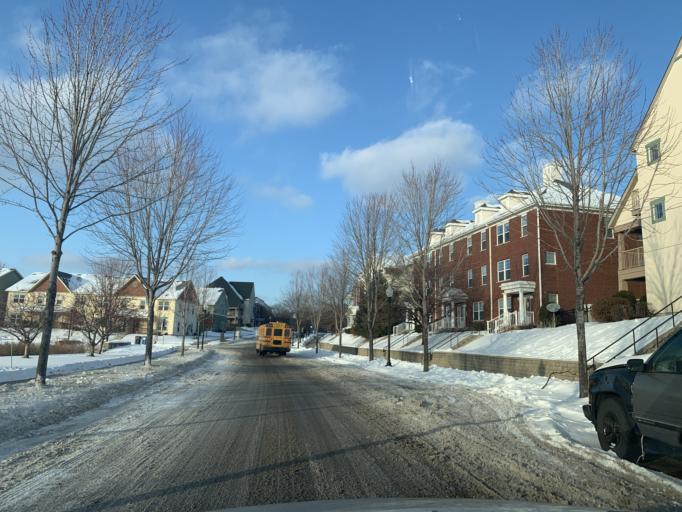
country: US
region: Minnesota
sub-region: Hennepin County
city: Minneapolis
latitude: 44.9875
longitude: -93.2909
